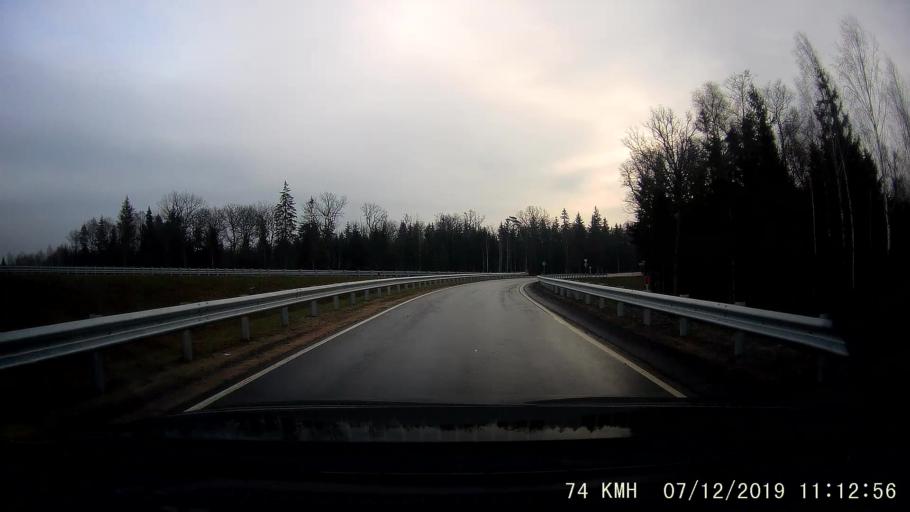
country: BY
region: Grodnenskaya
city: Iwye
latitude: 53.8804
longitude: 25.7385
